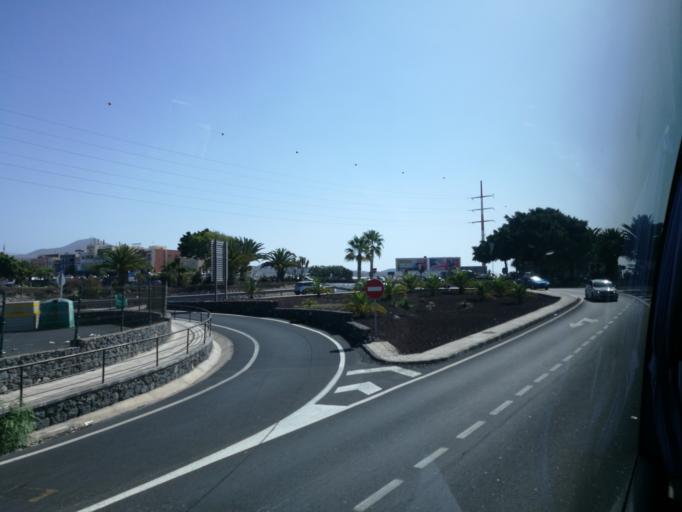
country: ES
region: Canary Islands
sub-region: Provincia de Santa Cruz de Tenerife
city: San Miguel
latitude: 28.0507
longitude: -16.6129
